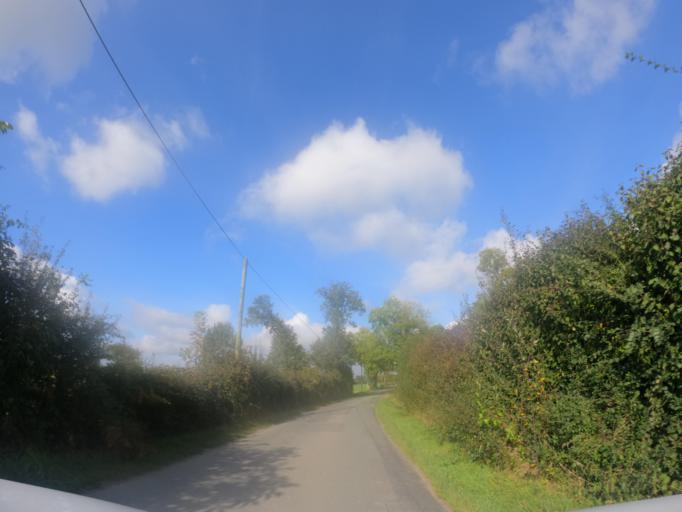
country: FR
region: Poitou-Charentes
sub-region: Departement des Deux-Sevres
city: Courlay
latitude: 46.7762
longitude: -0.5890
